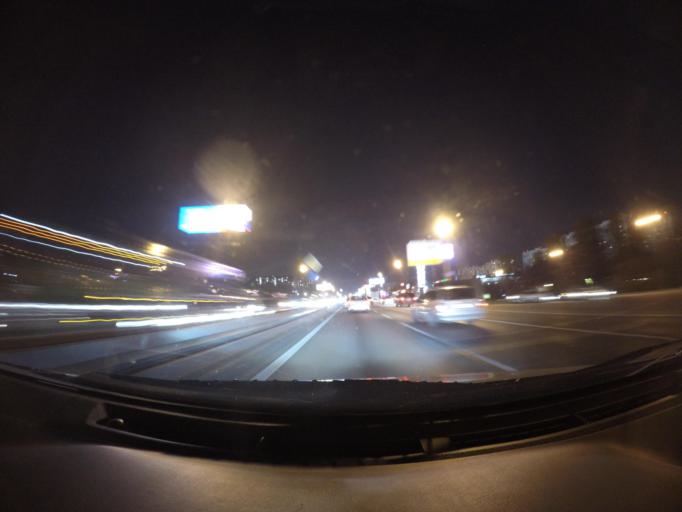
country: RU
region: Moscow
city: Khimki
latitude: 55.8916
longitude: 37.4342
